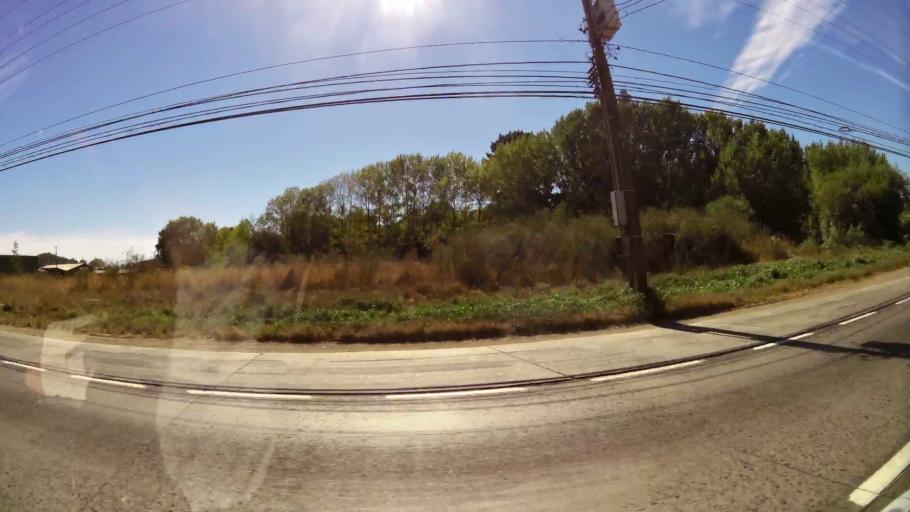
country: CL
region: Biobio
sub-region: Provincia de Concepcion
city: Penco
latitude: -36.7751
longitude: -73.0167
